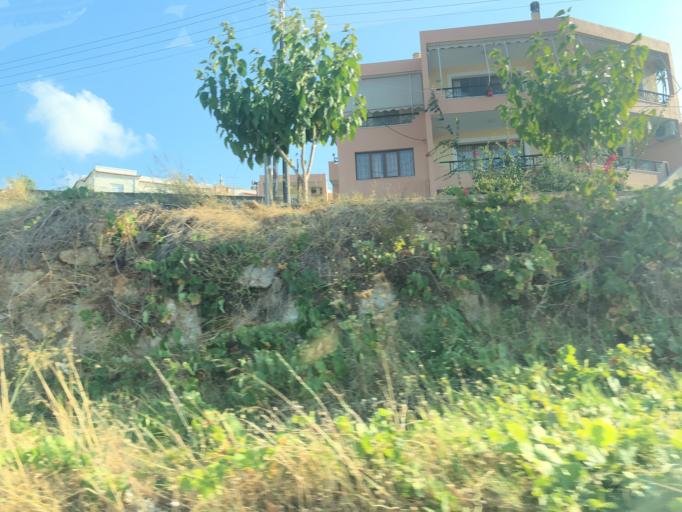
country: GR
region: Crete
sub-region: Nomos Rethymnis
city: Atsipopoulon
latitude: 35.3646
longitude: 24.4402
